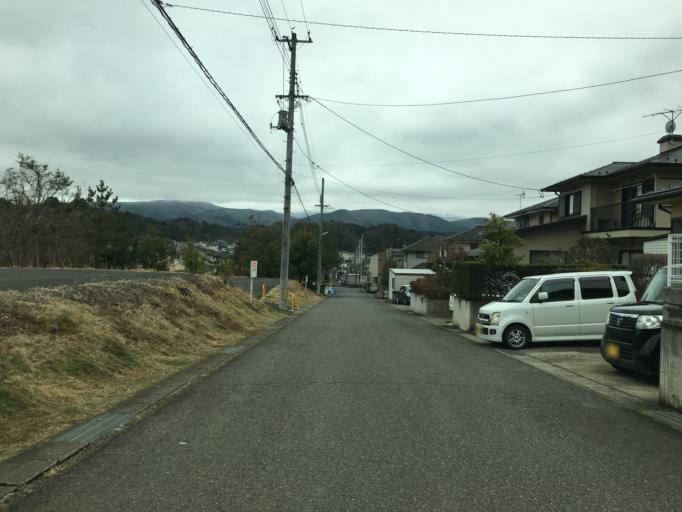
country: JP
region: Fukushima
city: Fukushima-shi
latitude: 37.7210
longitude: 140.4108
